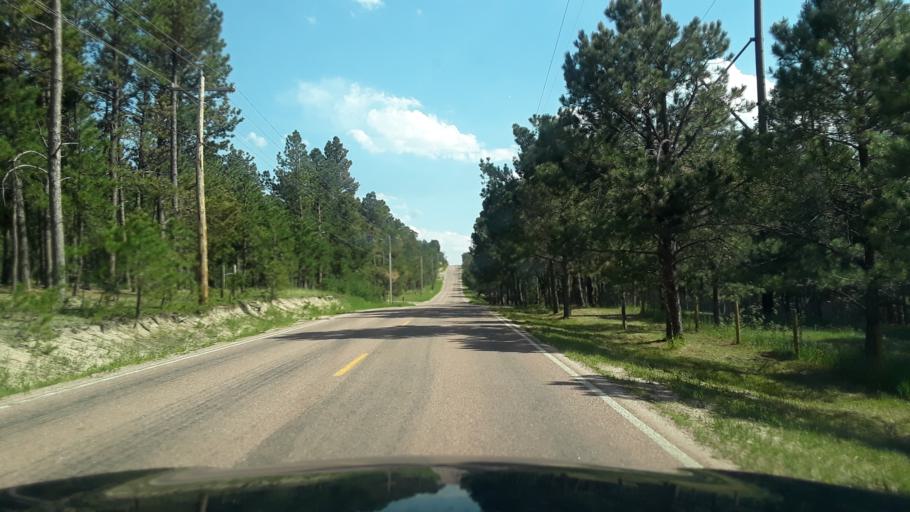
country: US
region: Colorado
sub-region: El Paso County
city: Gleneagle
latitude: 39.0544
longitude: -104.7849
